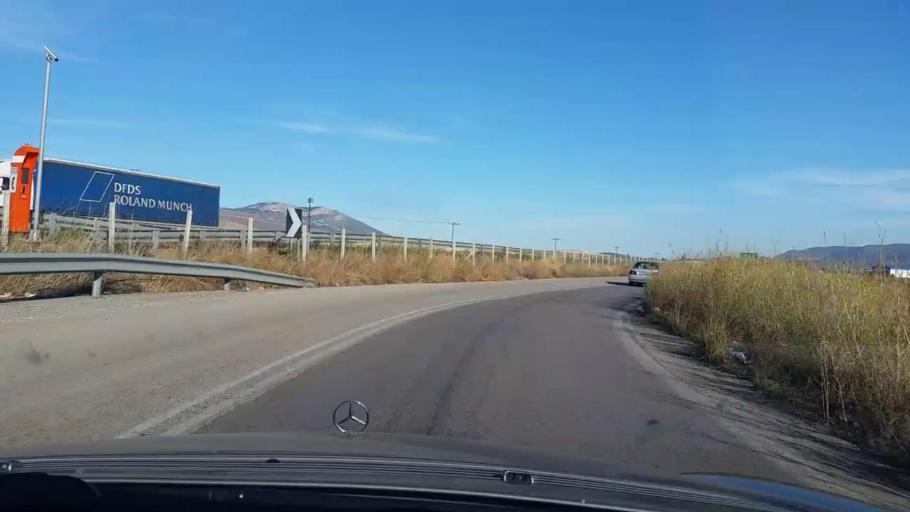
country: GR
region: Central Greece
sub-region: Nomos Voiotias
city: Thivai
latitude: 38.3671
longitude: 23.3021
